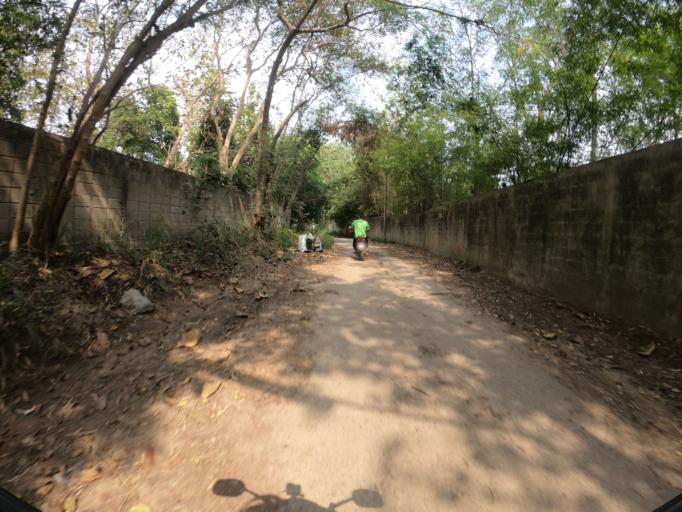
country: TH
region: Chiang Mai
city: Chiang Mai
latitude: 18.7510
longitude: 98.9369
